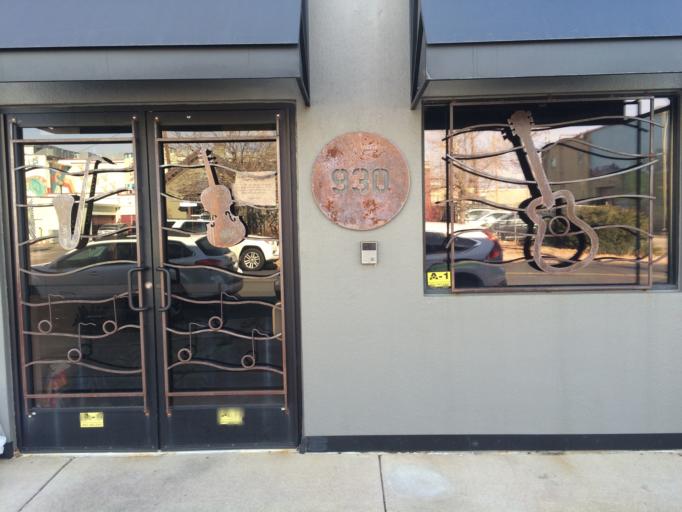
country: US
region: Colorado
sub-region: Denver County
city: Denver
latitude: 39.7273
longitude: -104.9993
